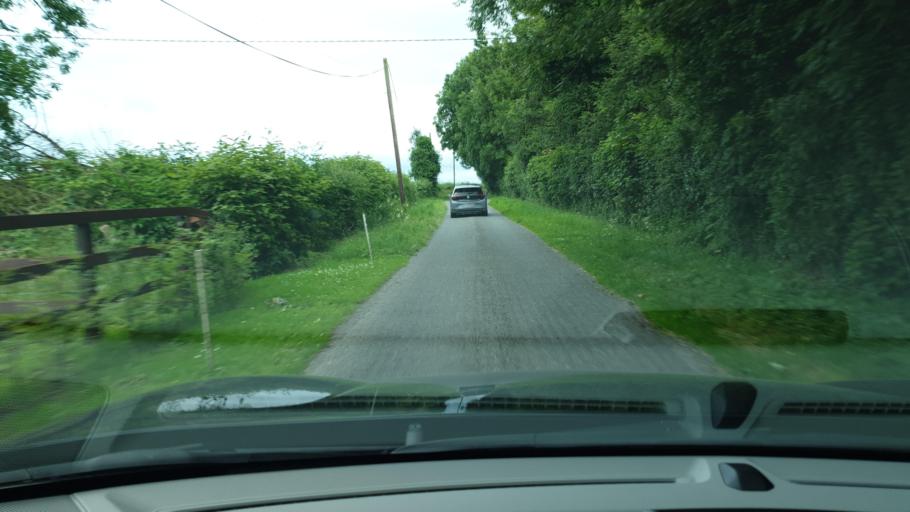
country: IE
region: Leinster
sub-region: An Mhi
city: Dunshaughlin
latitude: 53.5286
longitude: -6.5211
